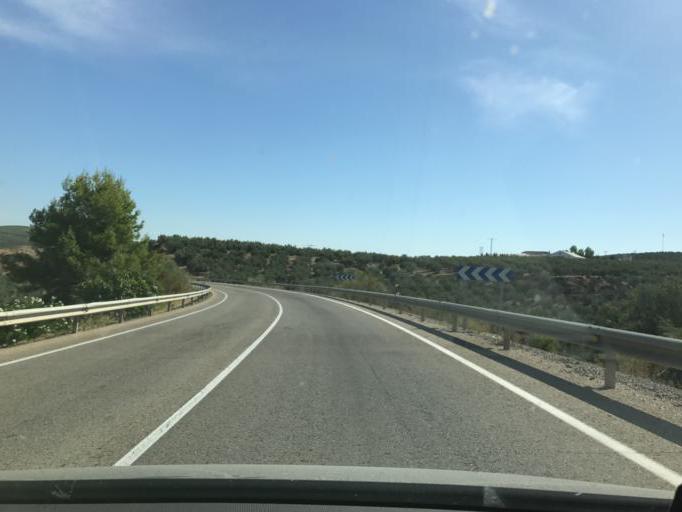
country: ES
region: Andalusia
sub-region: Province of Cordoba
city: Castro del Rio
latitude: 37.6662
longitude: -4.3996
